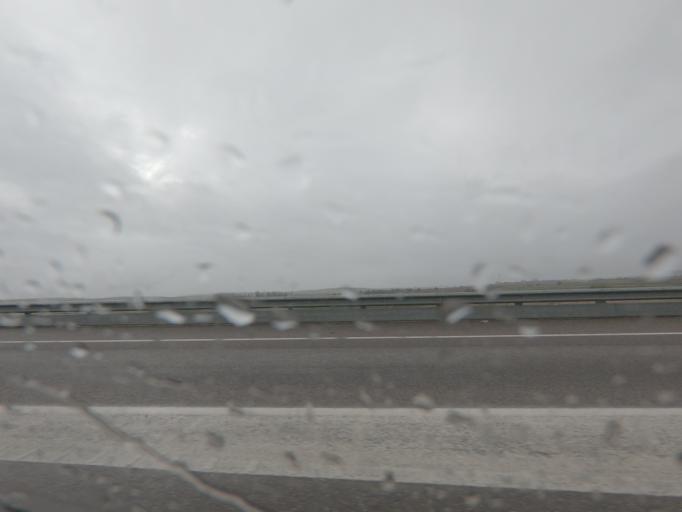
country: ES
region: Extremadura
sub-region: Provincia de Badajoz
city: Badajoz
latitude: 38.9151
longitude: -6.9632
